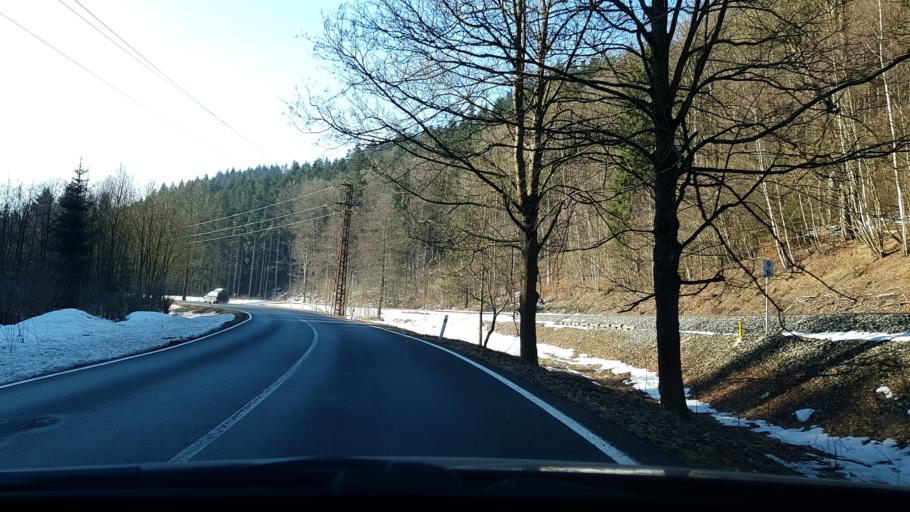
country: CZ
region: Olomoucky
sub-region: Okres Sumperk
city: Stare Mesto
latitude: 50.1250
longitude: 17.0084
